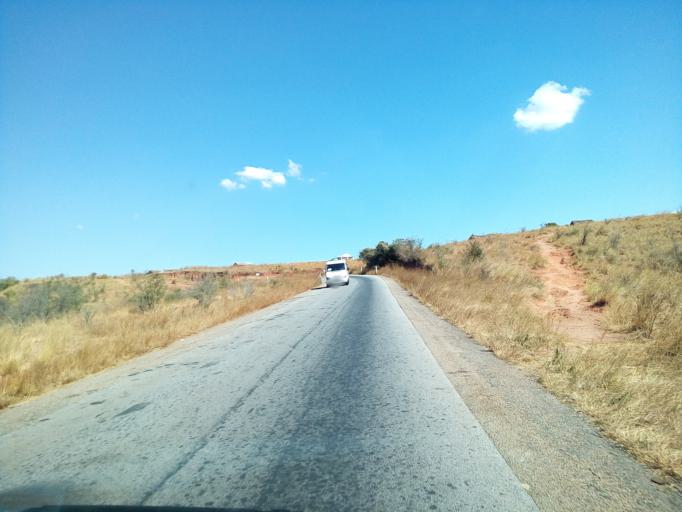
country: MG
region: Betsiboka
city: Maevatanana
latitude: -17.4186
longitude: 46.9194
